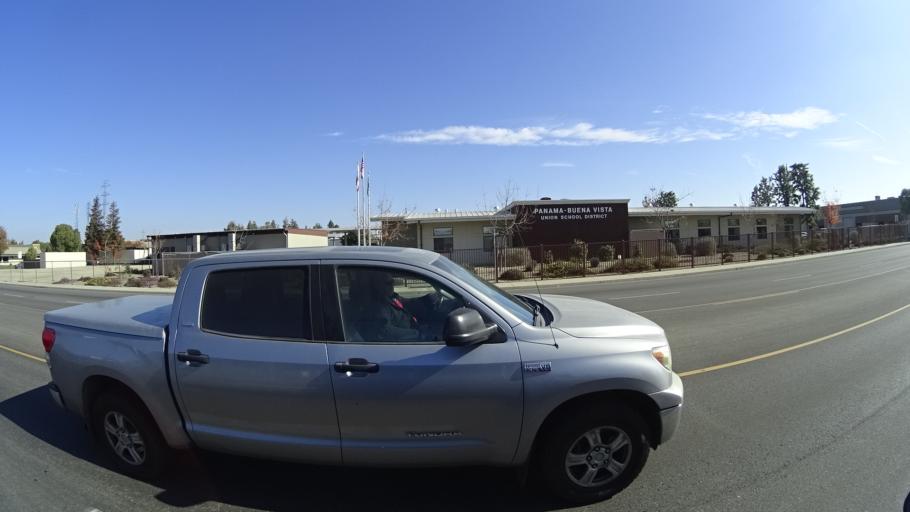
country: US
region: California
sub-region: Kern County
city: Greenacres
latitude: 35.3157
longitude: -119.0746
